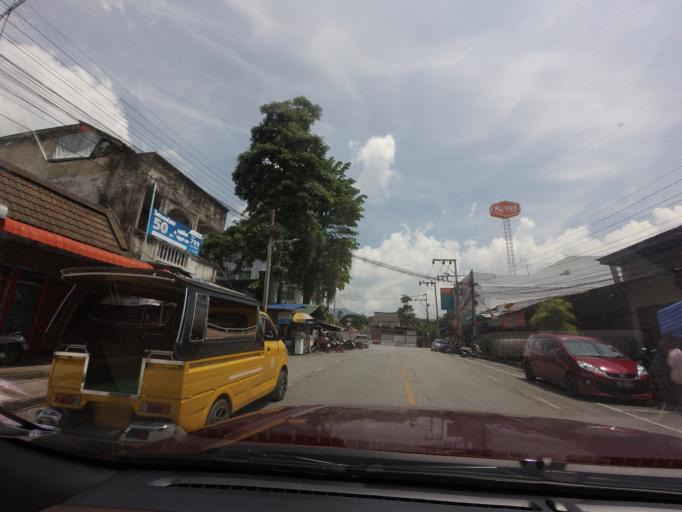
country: TH
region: Yala
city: Betong
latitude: 5.7731
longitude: 101.0677
